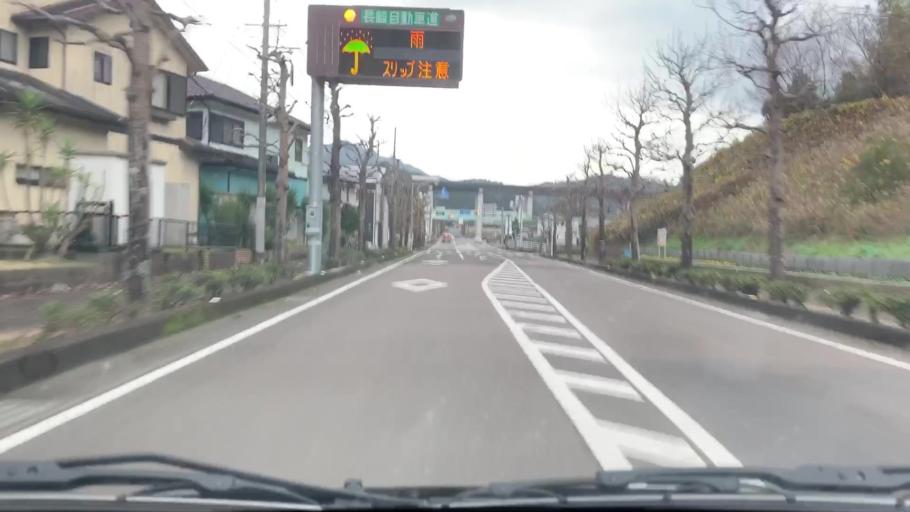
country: JP
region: Saga Prefecture
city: Ureshinomachi-shimojuku
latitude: 33.1077
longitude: 129.9773
